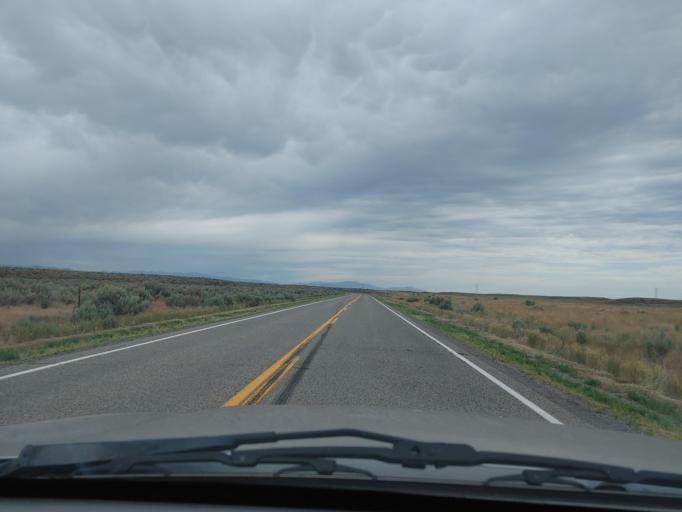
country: US
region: Idaho
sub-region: Lincoln County
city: Shoshone
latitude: 43.0764
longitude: -114.1048
